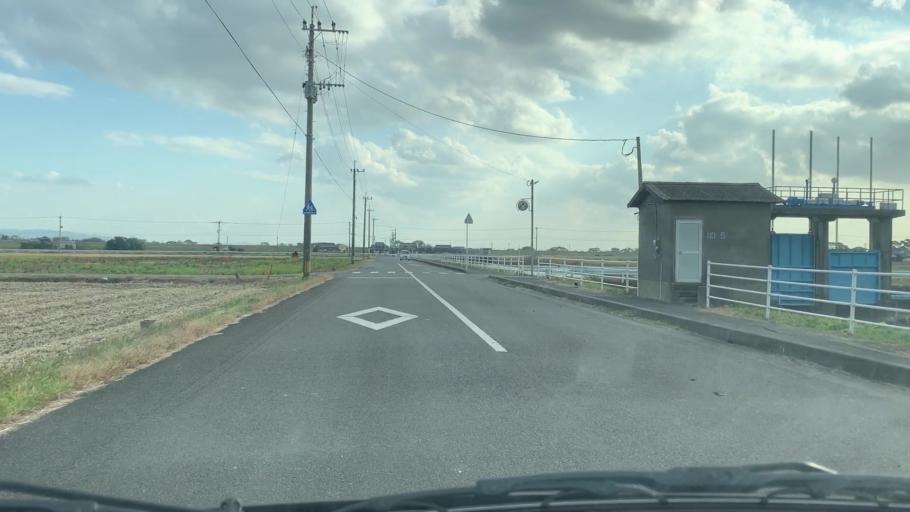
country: JP
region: Saga Prefecture
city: Kanzakimachi-kanzaki
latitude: 33.2816
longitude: 130.4411
